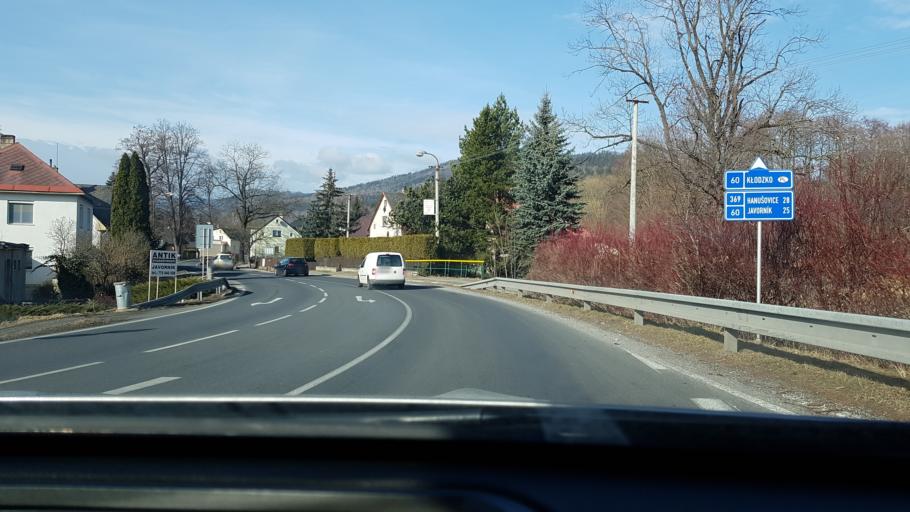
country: CZ
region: Olomoucky
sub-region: Okres Jesenik
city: Jesenik
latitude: 50.2286
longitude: 17.1570
